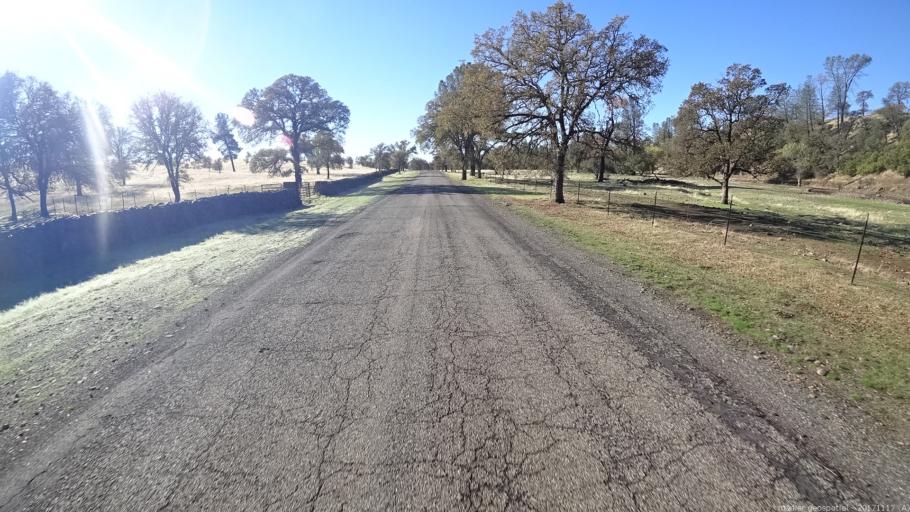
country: US
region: California
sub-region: Shasta County
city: Cottonwood
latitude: 40.4406
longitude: -122.1623
